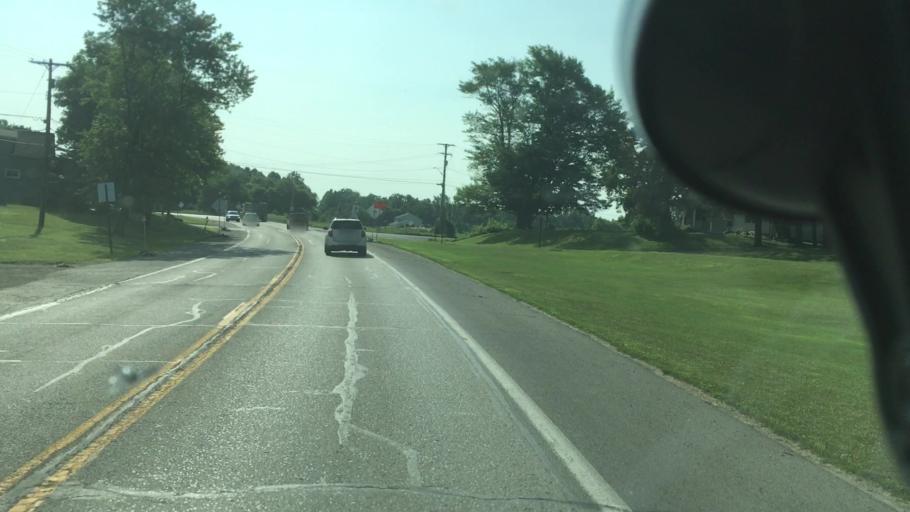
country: US
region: Pennsylvania
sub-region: Lawrence County
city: Bessemer
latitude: 41.0075
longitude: -80.4664
